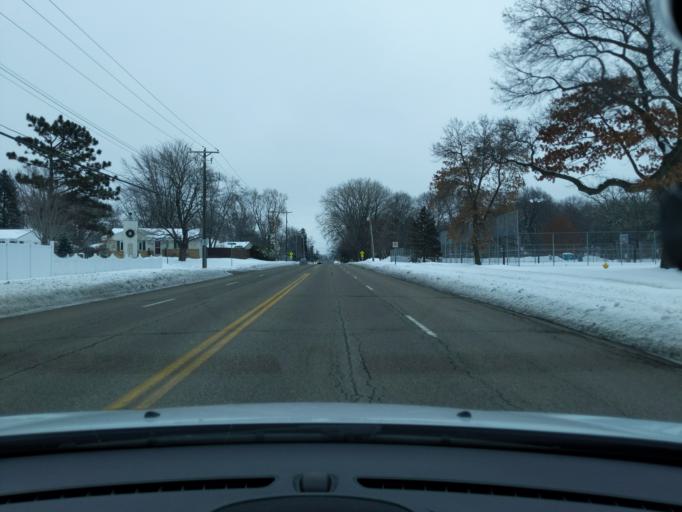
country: US
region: Minnesota
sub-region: Ramsey County
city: Little Canada
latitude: 45.0207
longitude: -93.1131
